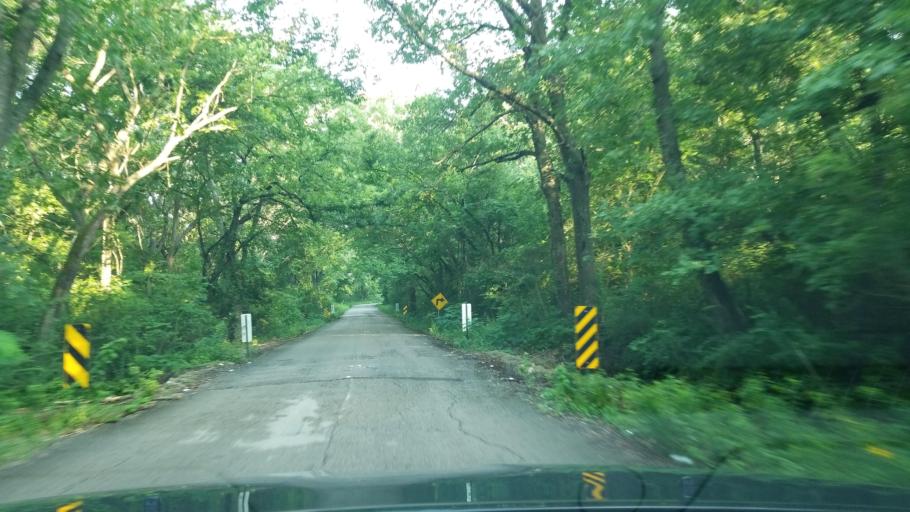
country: US
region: Texas
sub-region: Denton County
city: Cross Roads
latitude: 33.2578
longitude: -97.0624
